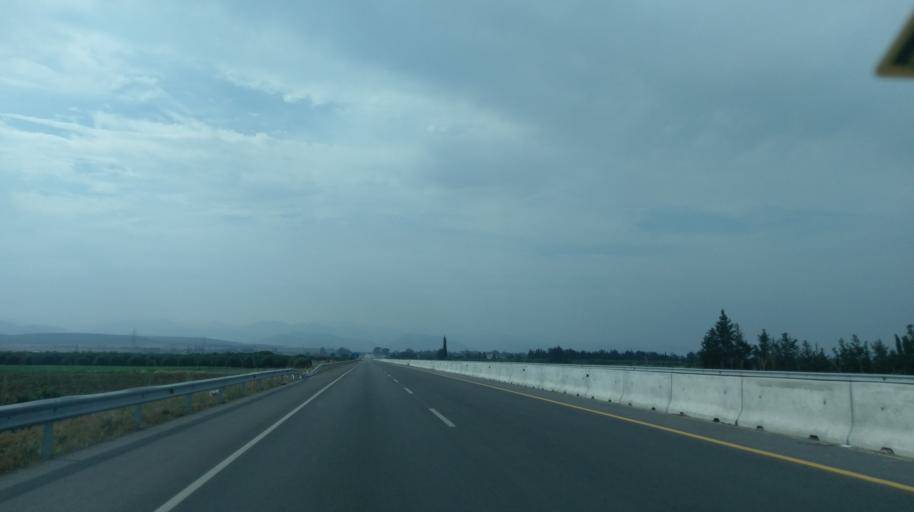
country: CY
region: Lefkosia
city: Lefka
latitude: 35.1574
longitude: 32.9157
